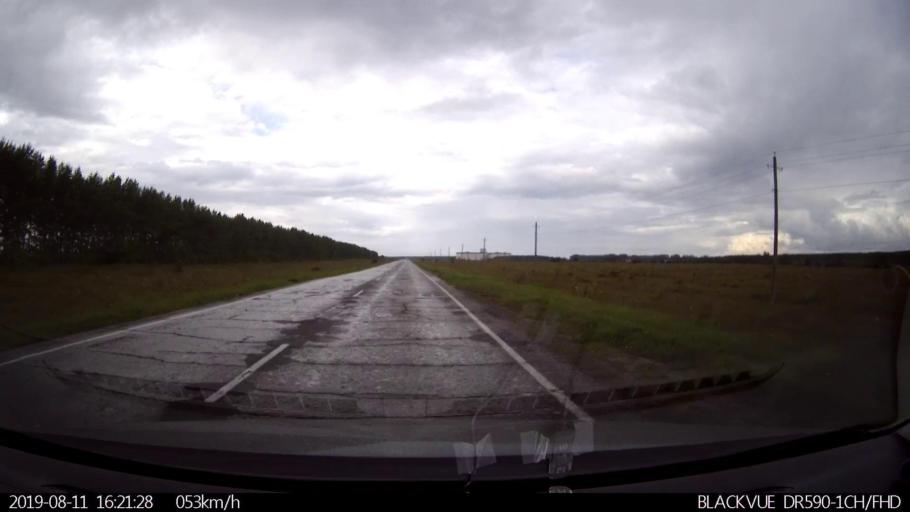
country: RU
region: Ulyanovsk
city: Mayna
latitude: 54.0801
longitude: 47.5978
